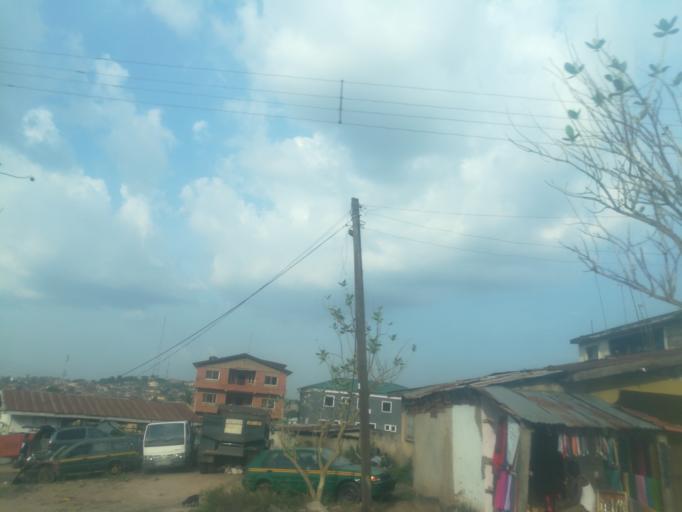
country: NG
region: Ogun
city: Abeokuta
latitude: 7.1434
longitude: 3.3285
